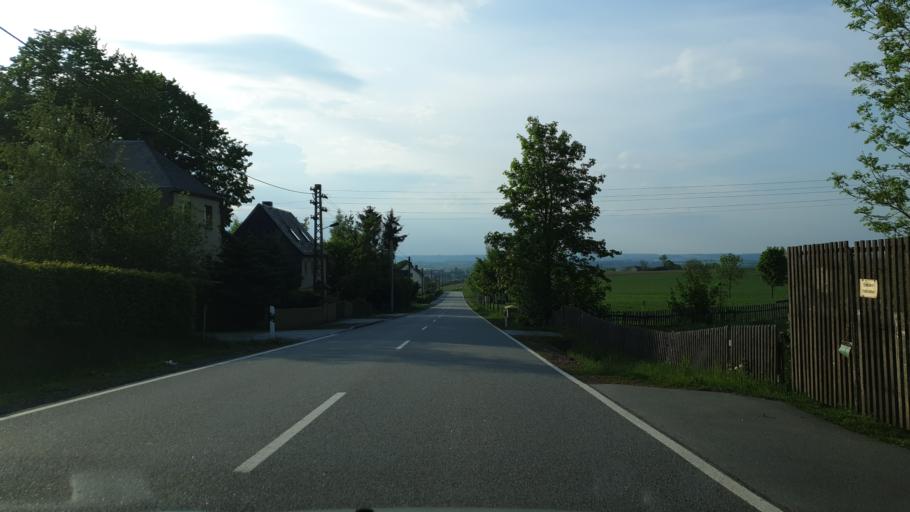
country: DE
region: Saxony
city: Stollberg
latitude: 50.6989
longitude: 12.7926
